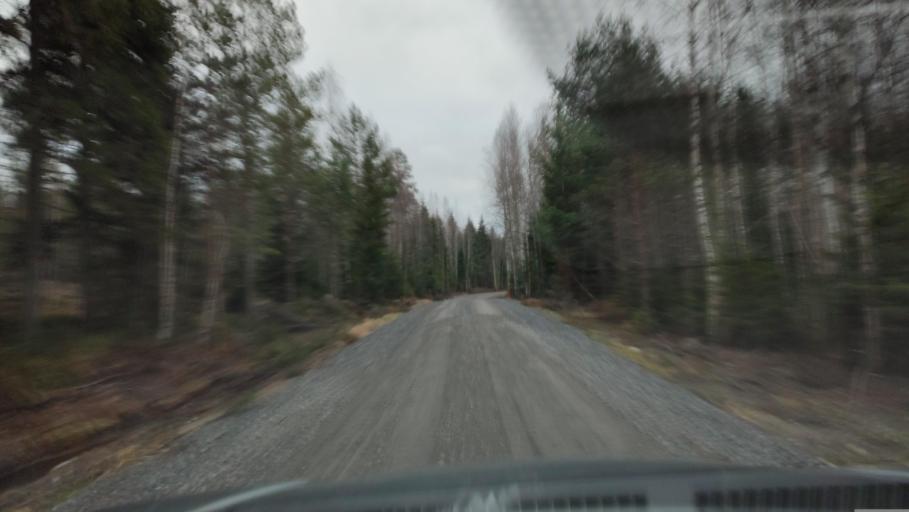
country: FI
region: Southern Ostrobothnia
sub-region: Suupohja
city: Karijoki
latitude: 62.2145
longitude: 21.6020
